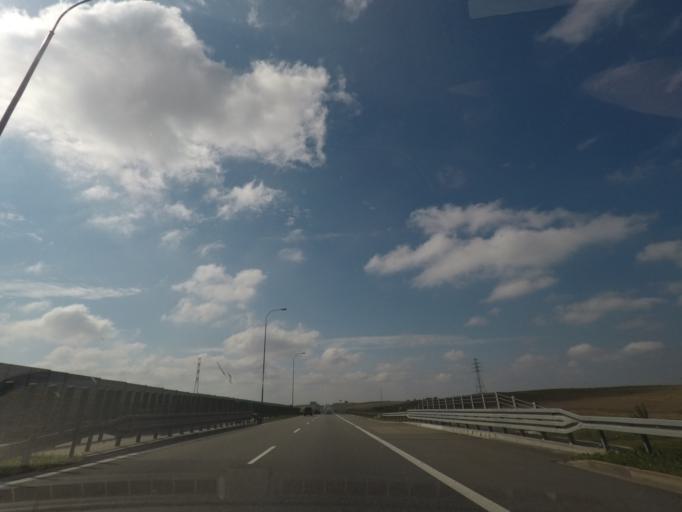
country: PL
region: Kujawsko-Pomorskie
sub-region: Powiat chelminski
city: Lisewo
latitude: 53.3352
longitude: 18.7089
